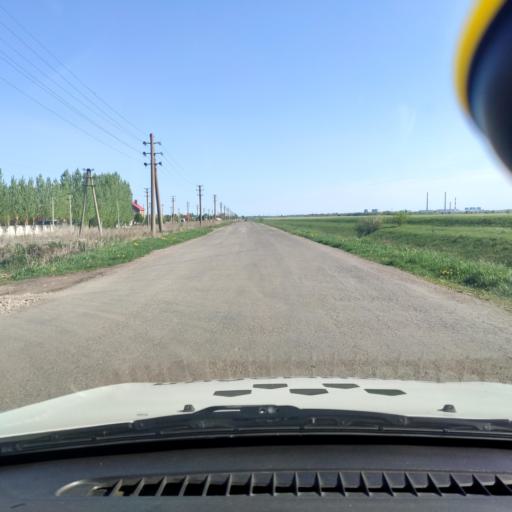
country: RU
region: Samara
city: Podstepki
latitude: 53.5248
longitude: 49.1971
